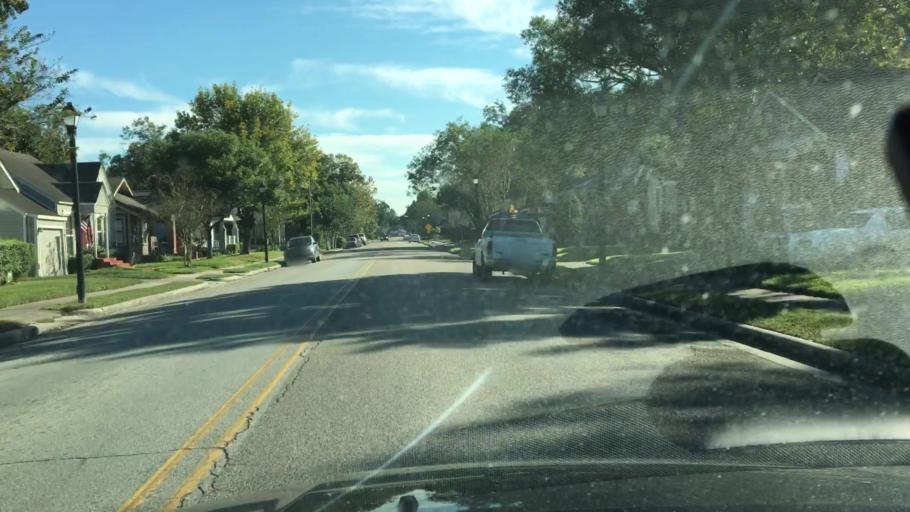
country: US
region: Texas
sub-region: Harris County
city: Houston
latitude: 29.7964
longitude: -95.3870
